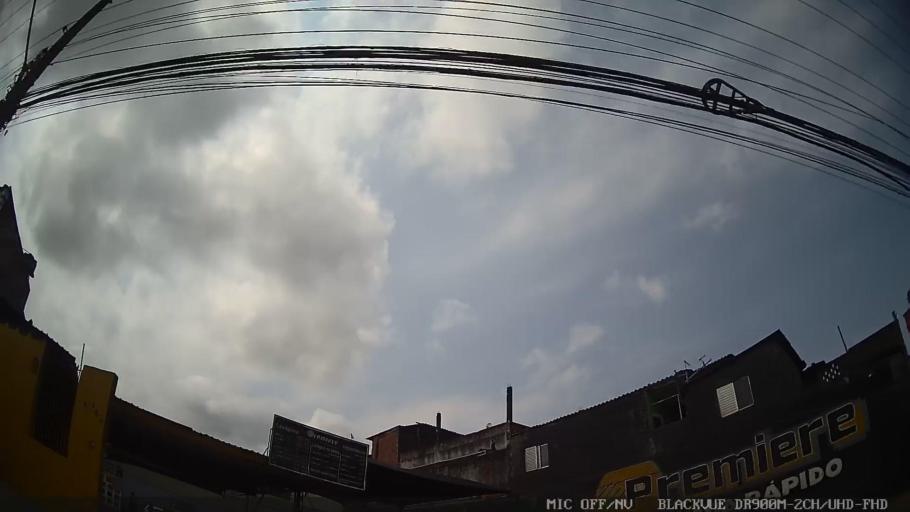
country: BR
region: Sao Paulo
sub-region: Taboao Da Serra
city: Taboao da Serra
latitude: -23.6661
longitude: -46.7163
